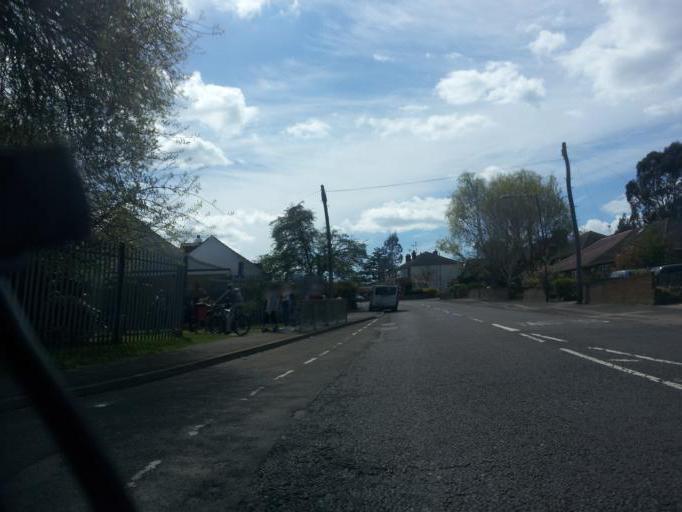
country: GB
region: England
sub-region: Kent
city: Rainham
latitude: 51.3508
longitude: 0.5805
